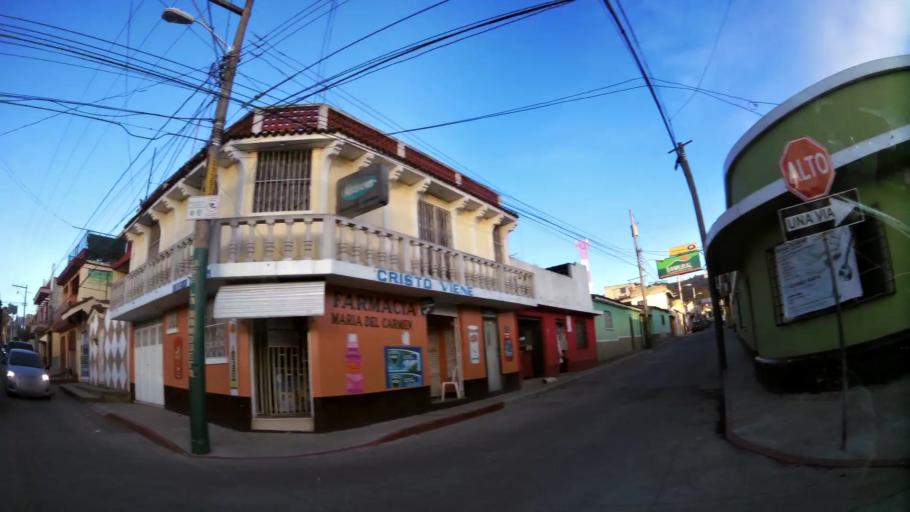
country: GT
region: Sacatepequez
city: San Lucas Sacatepequez
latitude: 14.6124
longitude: -90.6555
